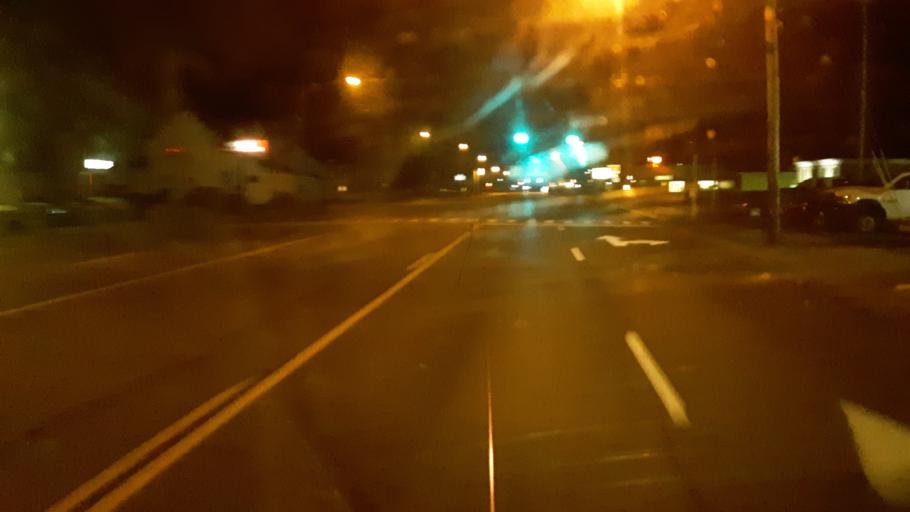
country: US
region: New York
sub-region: Oneida County
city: Rome
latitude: 43.2277
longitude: -75.4905
